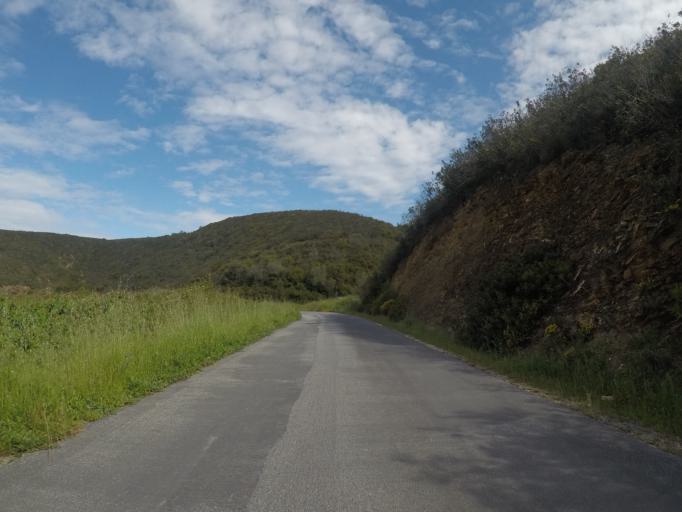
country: PT
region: Beja
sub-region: Odemira
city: Sao Teotonio
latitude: 37.4374
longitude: -8.7874
